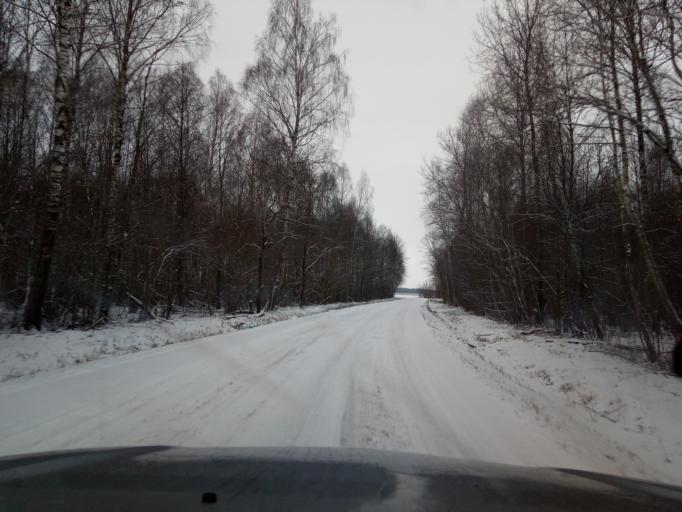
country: LT
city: Ramygala
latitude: 55.4902
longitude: 24.5568
